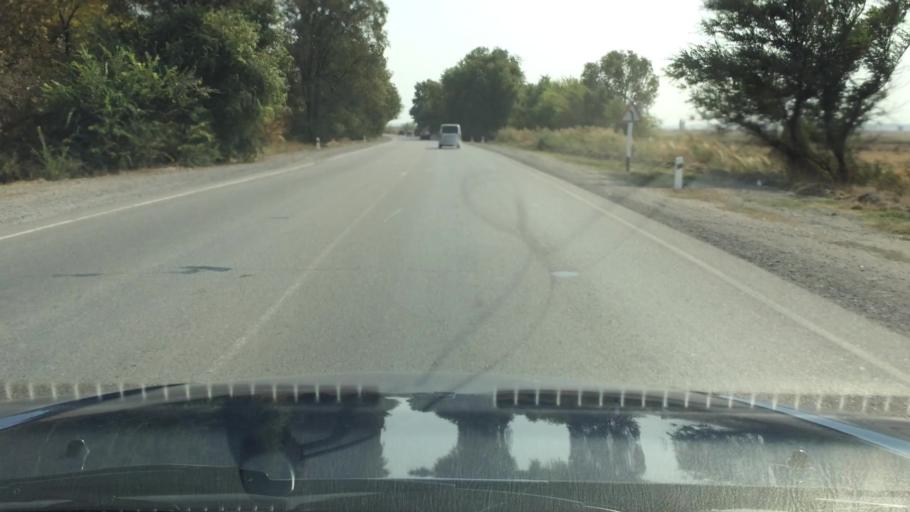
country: KG
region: Chuy
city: Lebedinovka
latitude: 42.9229
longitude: 74.7055
